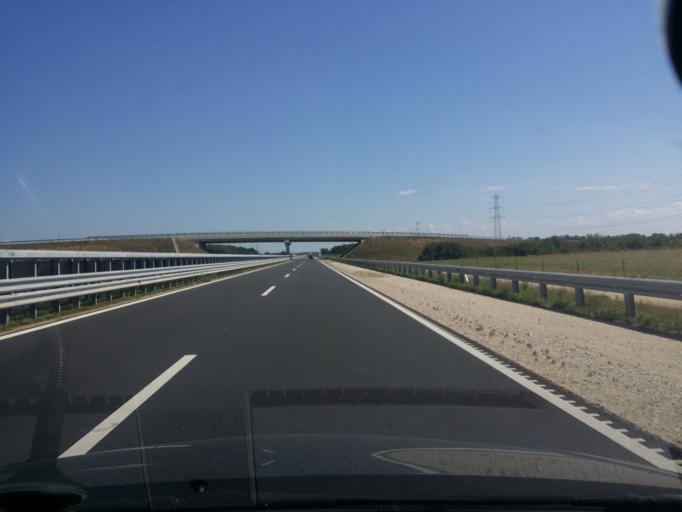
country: HU
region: Vas
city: Repcelak
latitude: 47.3692
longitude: 16.9321
